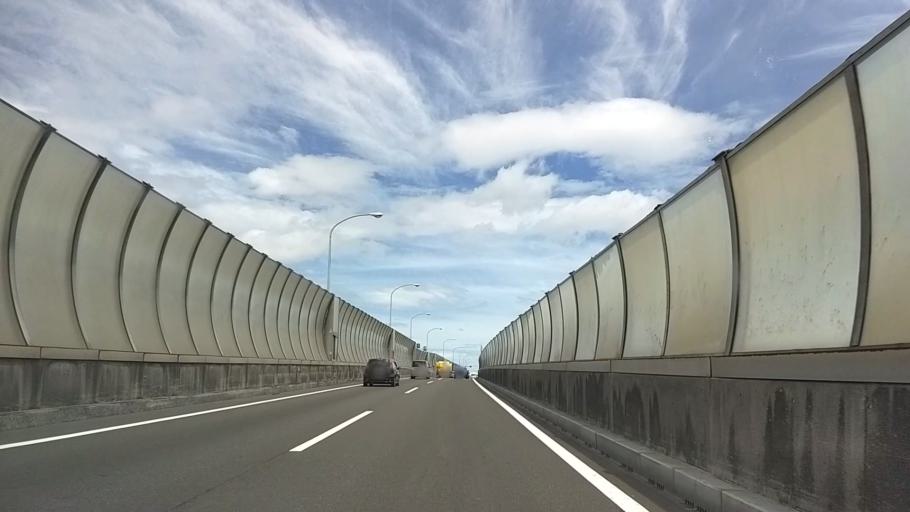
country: JP
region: Kanagawa
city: Minami-rinkan
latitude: 35.4969
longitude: 139.4941
